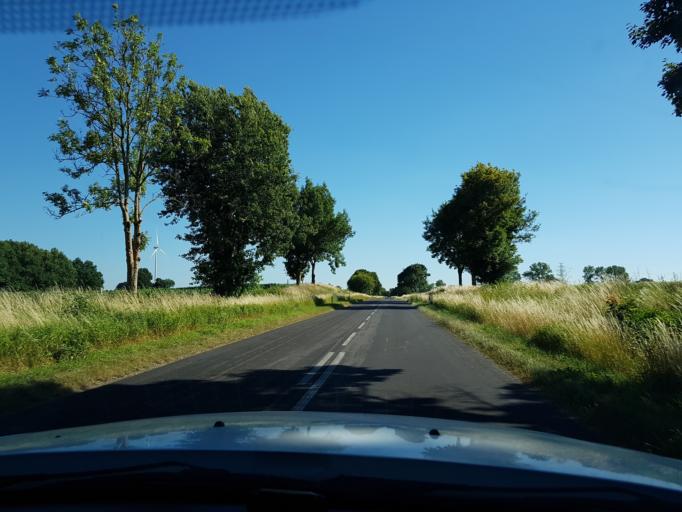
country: PL
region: West Pomeranian Voivodeship
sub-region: Powiat lobeski
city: Lobez
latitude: 53.6820
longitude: 15.6059
